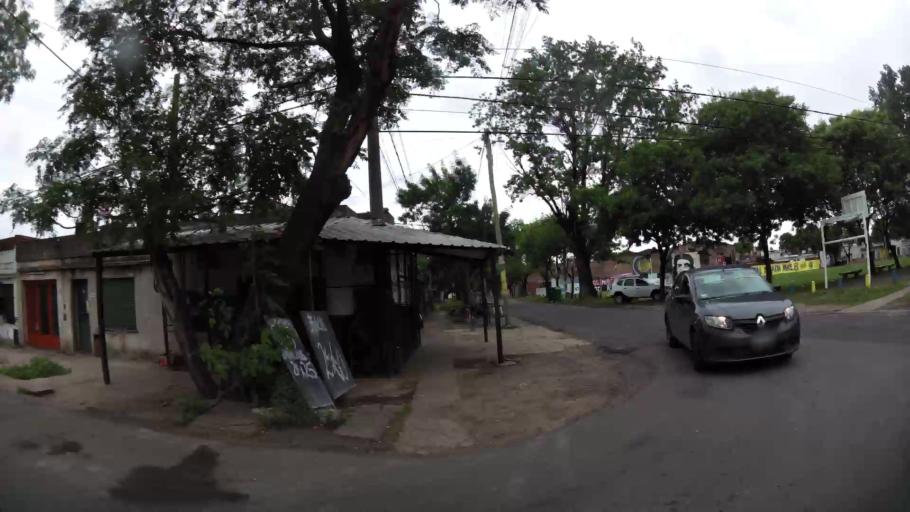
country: AR
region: Santa Fe
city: Gobernador Galvez
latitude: -32.9941
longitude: -60.6536
